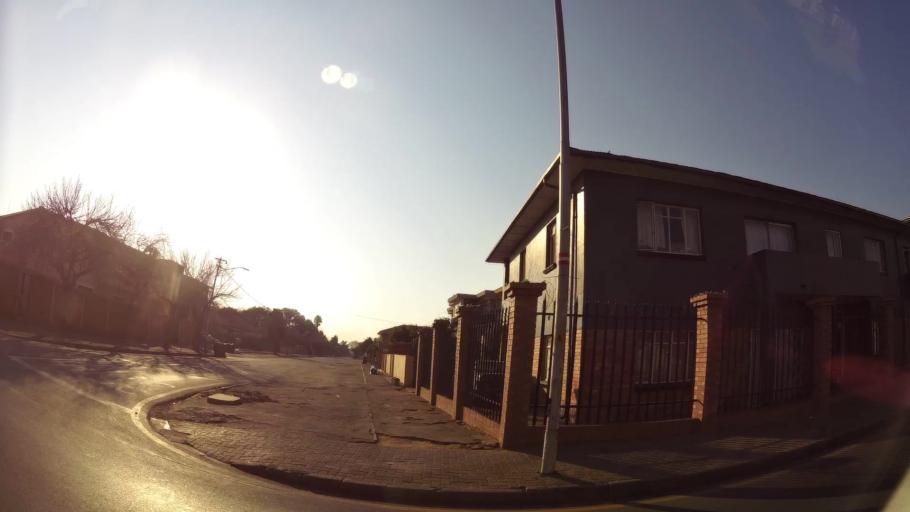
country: ZA
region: Gauteng
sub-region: Ekurhuleni Metropolitan Municipality
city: Germiston
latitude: -26.2255
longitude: 28.1663
